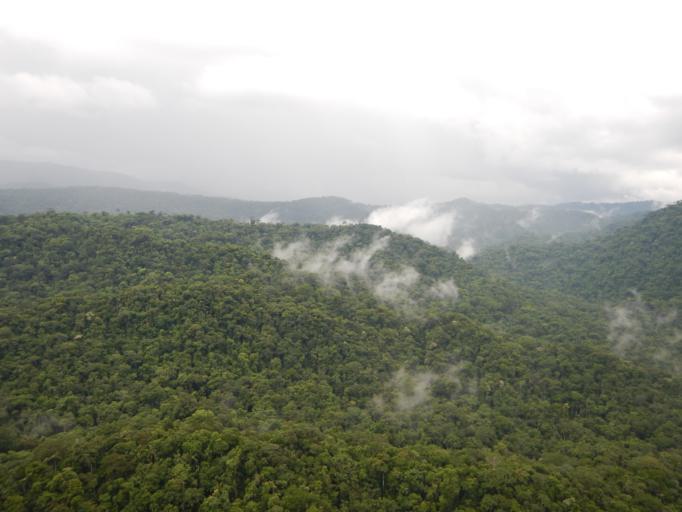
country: BO
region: Santa Cruz
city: Comarapa
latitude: -17.3968
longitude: -64.4406
